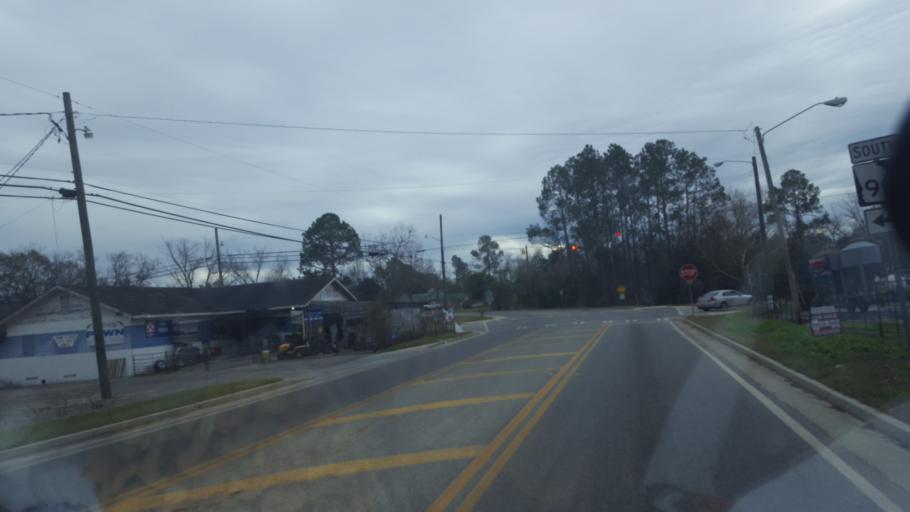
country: US
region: Georgia
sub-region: Ben Hill County
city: Fitzgerald
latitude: 31.7243
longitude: -83.2608
